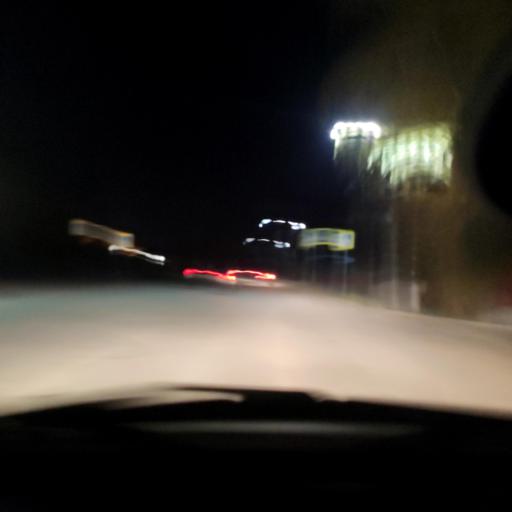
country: RU
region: Bashkortostan
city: Iglino
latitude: 54.8322
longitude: 56.4076
